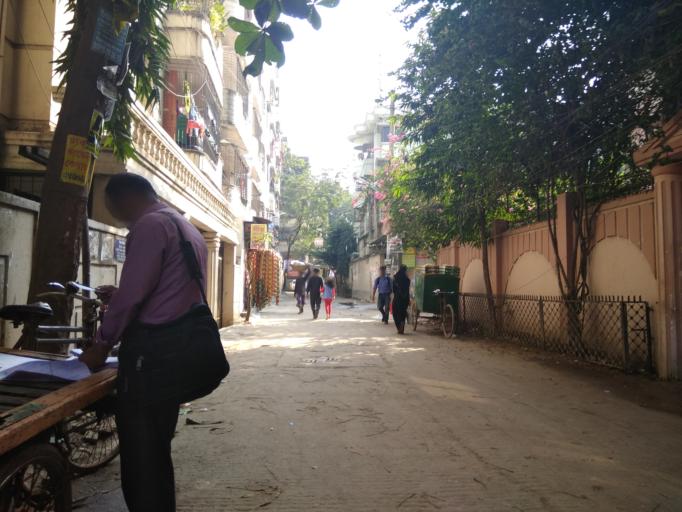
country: BD
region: Dhaka
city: Azimpur
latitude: 23.7632
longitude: 90.3553
